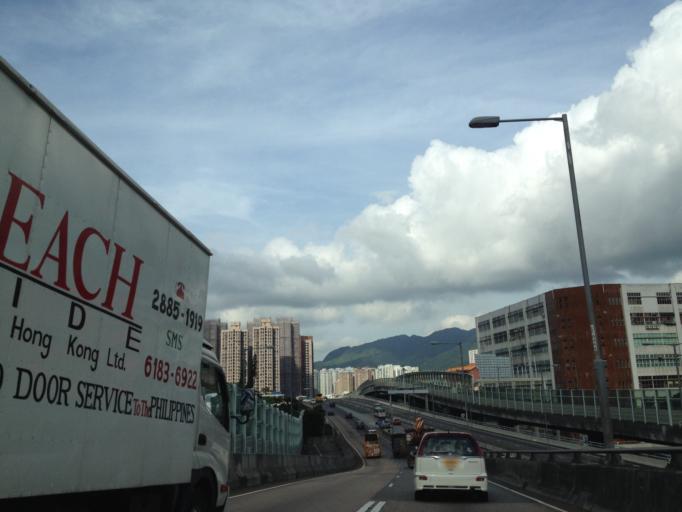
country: HK
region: Sha Tin
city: Sha Tin
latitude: 22.3776
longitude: 114.1807
